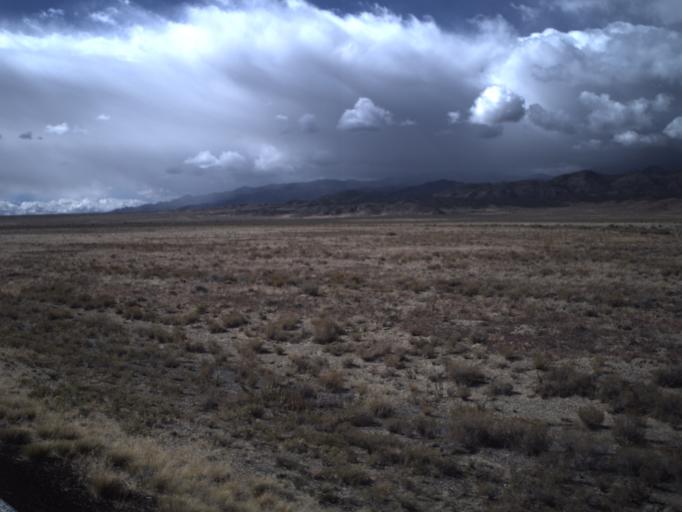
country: US
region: Nevada
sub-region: White Pine County
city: McGill
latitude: 38.9627
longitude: -114.0336
